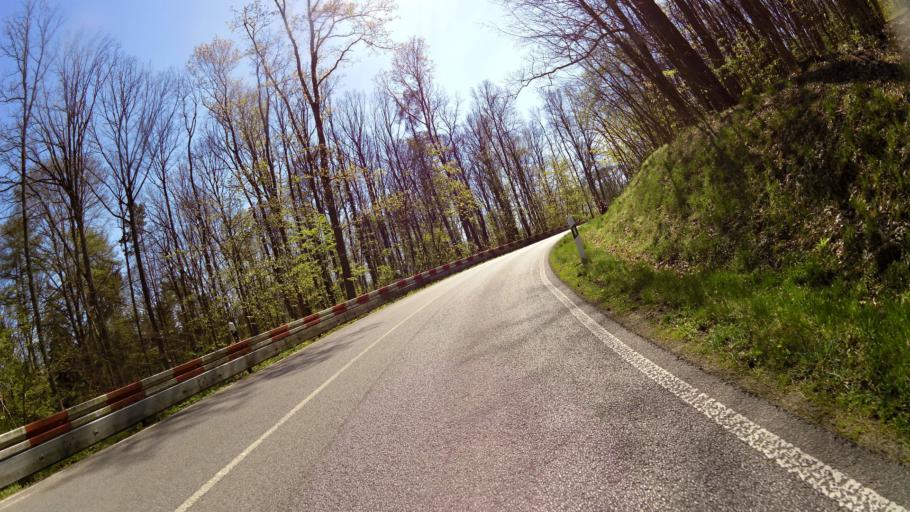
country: DE
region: Brandenburg
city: Buckow
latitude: 52.5825
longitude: 14.0670
